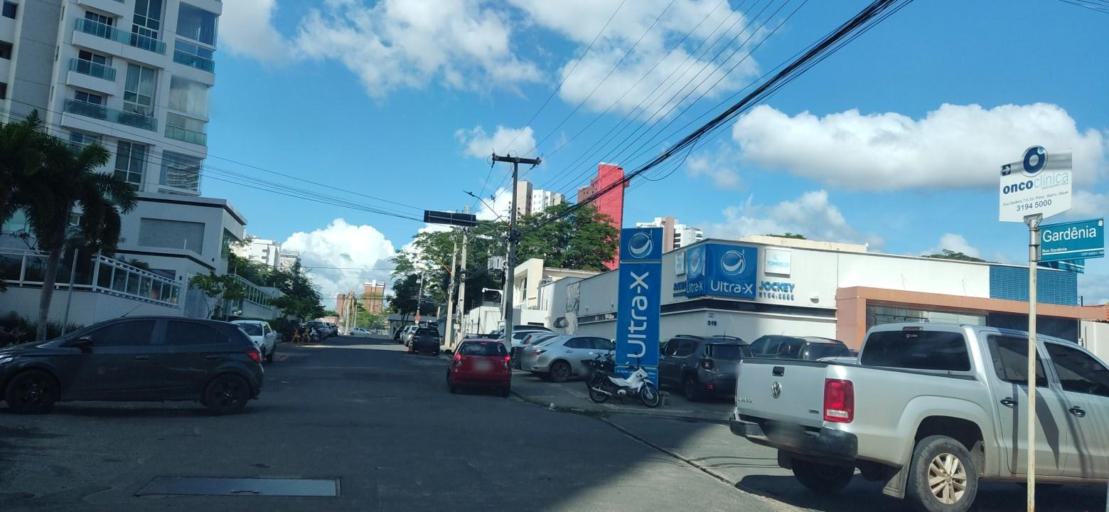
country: BR
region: Piaui
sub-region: Teresina
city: Teresina
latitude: -5.0776
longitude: -42.7914
